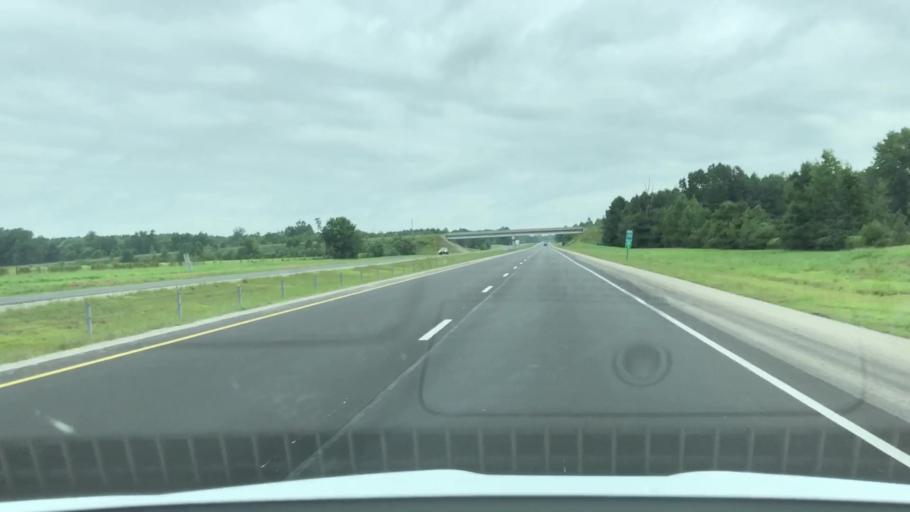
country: US
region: North Carolina
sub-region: Wilson County
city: Lucama
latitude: 35.6020
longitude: -77.9806
